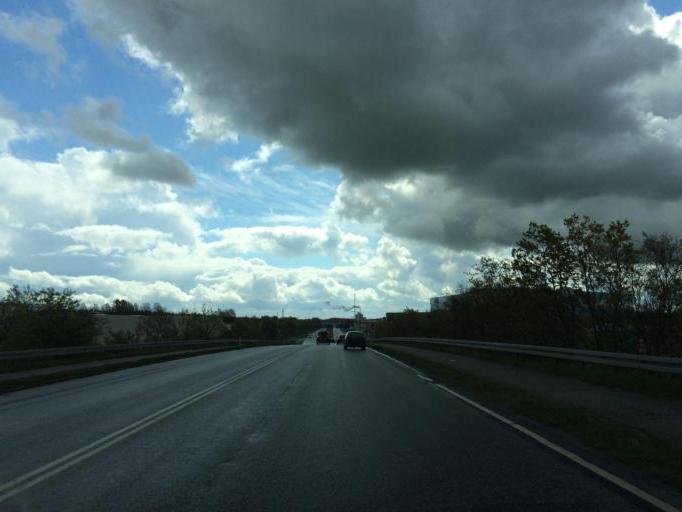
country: DK
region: Central Jutland
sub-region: Holstebro Kommune
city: Holstebro
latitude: 56.3743
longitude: 8.6226
